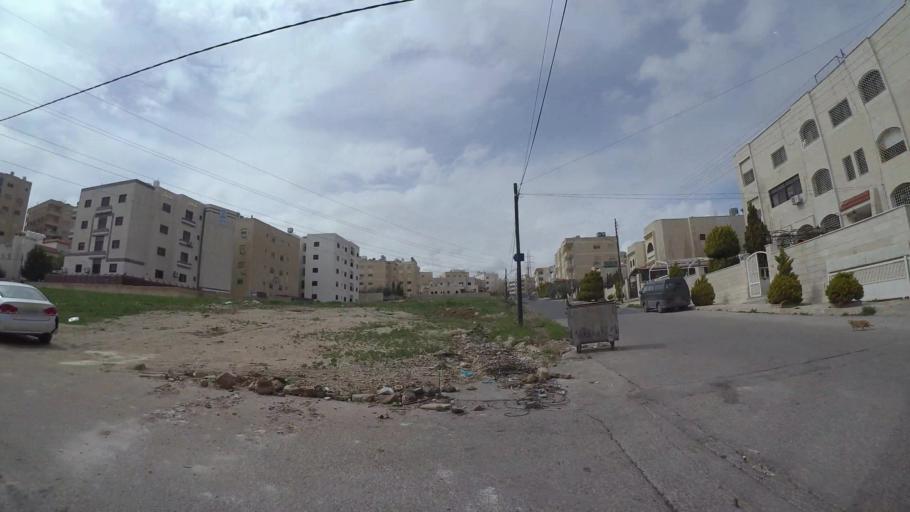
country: JO
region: Amman
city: Amman
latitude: 31.9965
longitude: 35.9371
